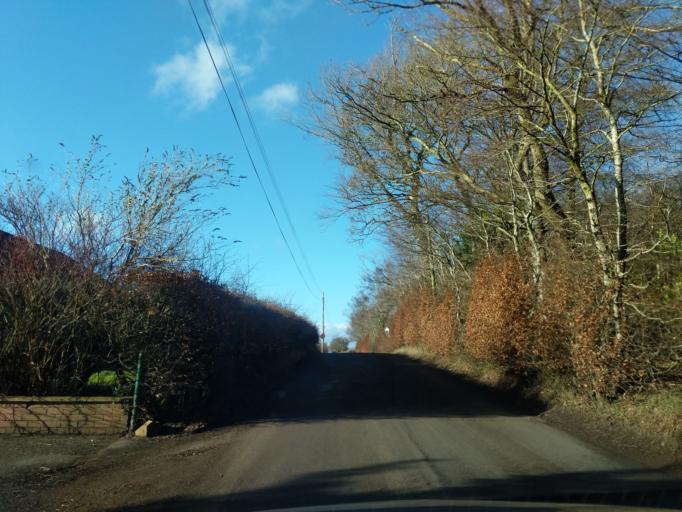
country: GB
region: Scotland
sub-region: South Lanarkshire
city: Carluke
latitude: 55.7106
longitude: -3.8483
